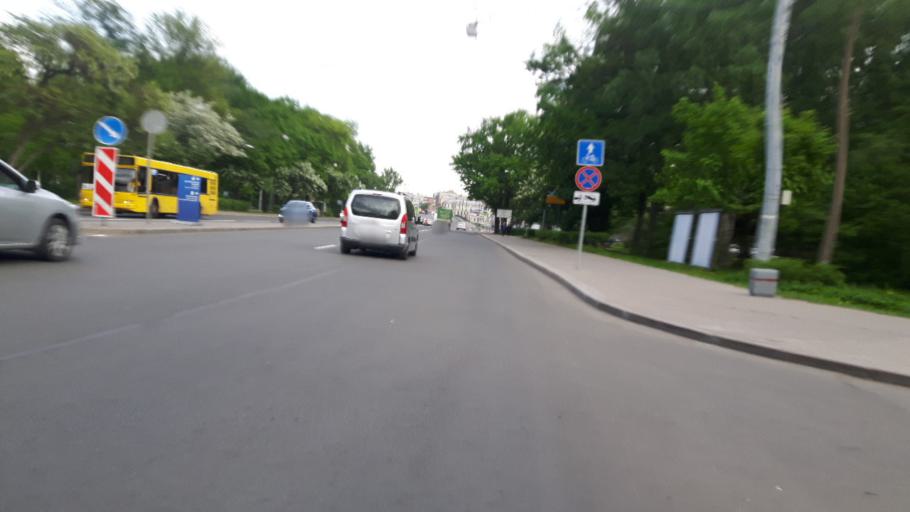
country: RU
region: Leningrad
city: Krestovskiy ostrov
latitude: 59.9696
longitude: 30.2758
